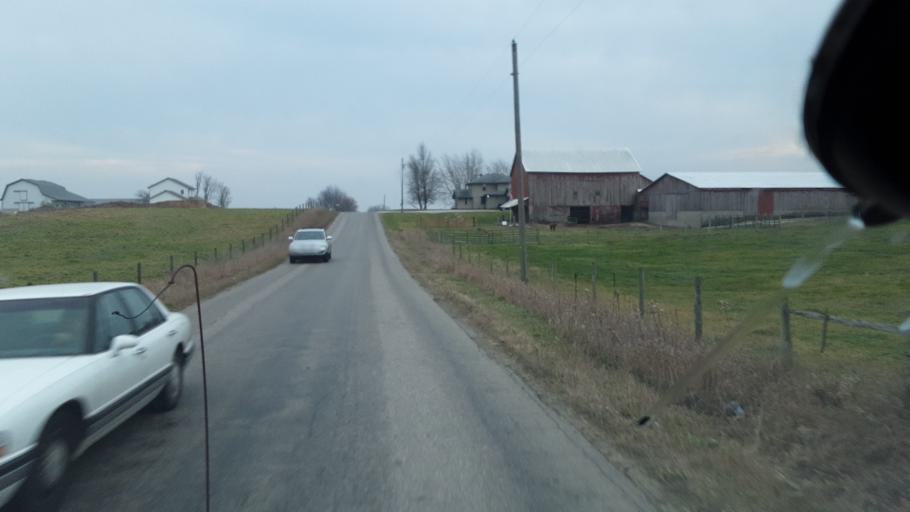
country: US
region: Michigan
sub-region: Saint Joseph County
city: White Pigeon
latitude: 41.7108
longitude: -85.6205
